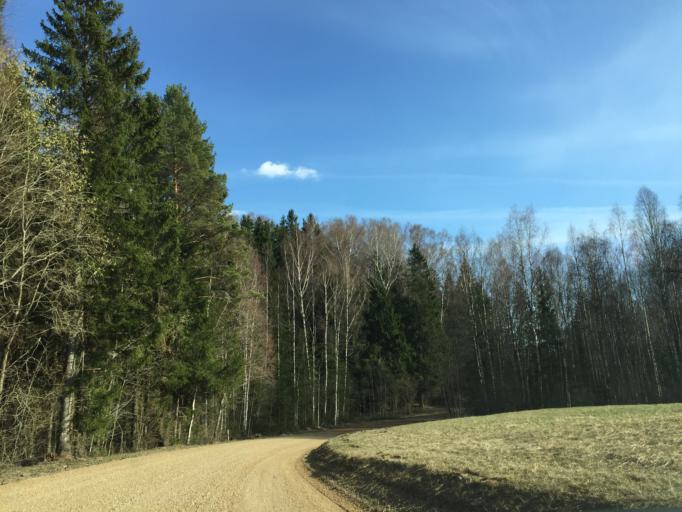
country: EE
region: Tartu
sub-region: Elva linn
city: Elva
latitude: 58.1035
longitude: 26.5051
